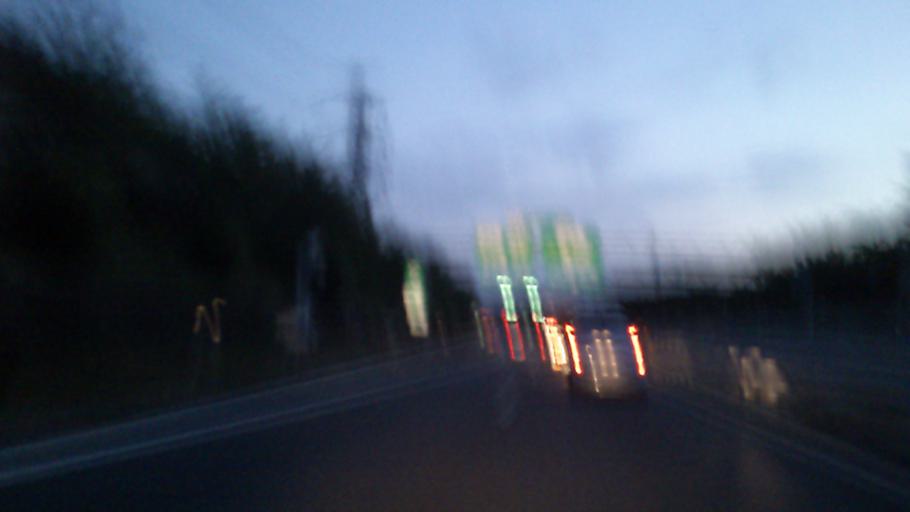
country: JP
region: Aichi
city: Kasugai
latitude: 35.2947
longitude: 136.9870
